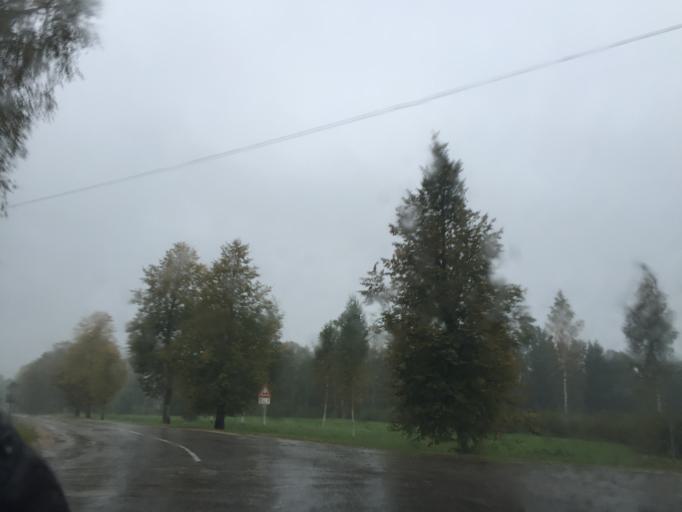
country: LV
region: Ropazu
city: Ropazi
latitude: 56.9817
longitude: 24.6311
